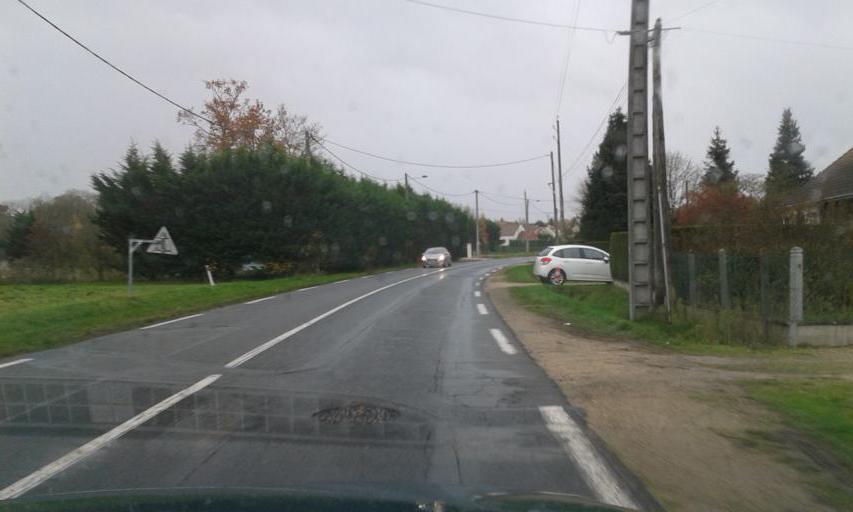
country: FR
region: Centre
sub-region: Departement du Loiret
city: Fay-aux-Loges
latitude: 47.9225
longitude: 2.1368
